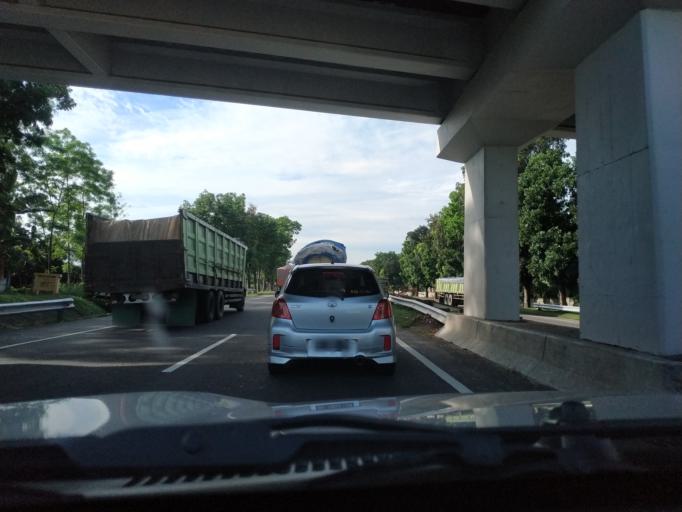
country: ID
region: North Sumatra
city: Deli Tua
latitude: 3.5516
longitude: 98.7251
